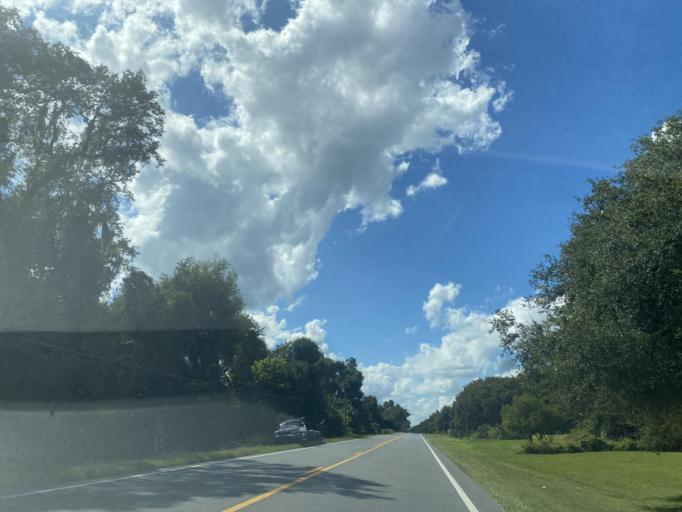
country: US
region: Florida
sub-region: Sumter County
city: The Villages
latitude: 28.9819
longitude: -81.9465
